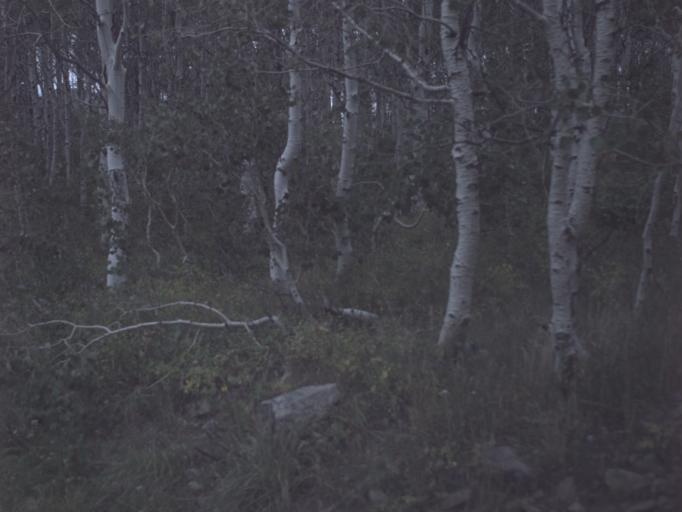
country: US
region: Utah
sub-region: Utah County
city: Lindon
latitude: 40.4336
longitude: -111.6153
